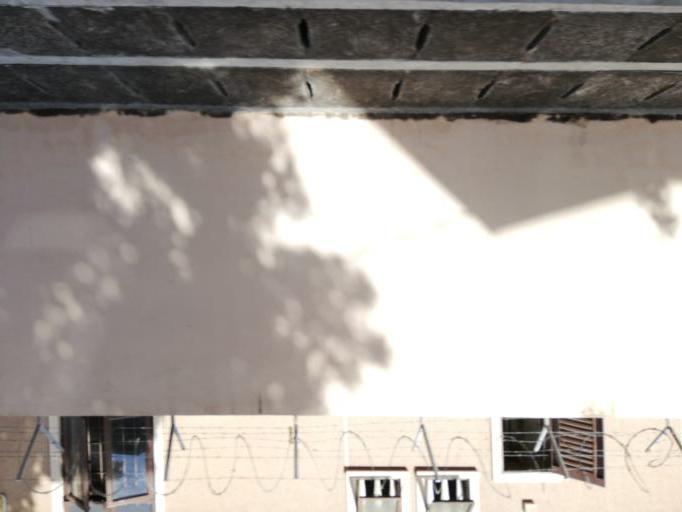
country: MU
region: Plaines Wilhems
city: Ebene
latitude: -20.2284
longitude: 57.4604
